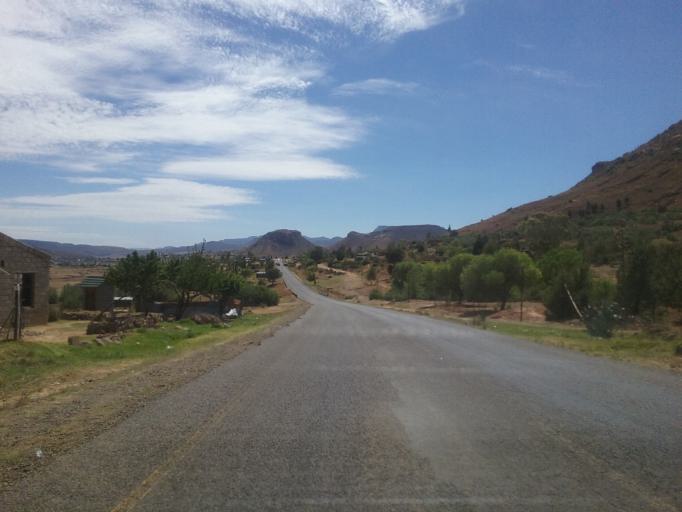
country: LS
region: Mohale's Hoek District
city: Mohale's Hoek
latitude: -30.1860
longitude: 27.4215
